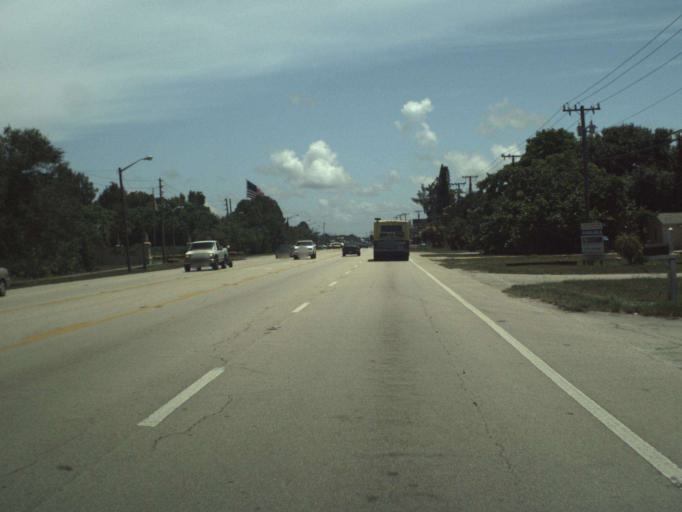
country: US
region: Florida
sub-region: Saint Lucie County
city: Fort Pierce South
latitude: 27.4050
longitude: -80.3260
